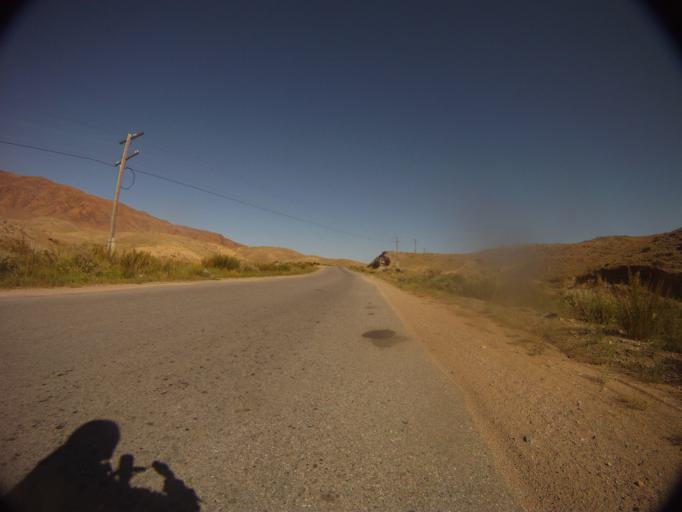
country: KG
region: Ysyk-Koel
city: Bokombayevskoye
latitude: 42.1408
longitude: 76.7611
